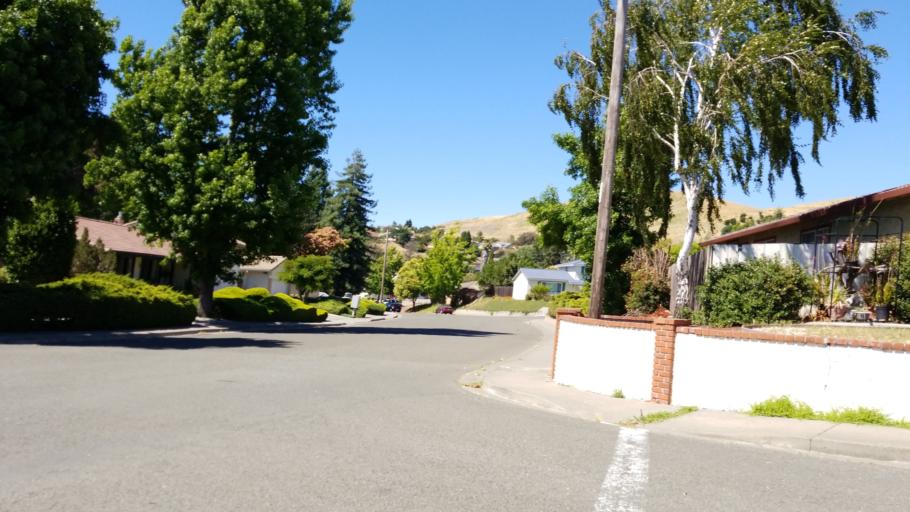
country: US
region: California
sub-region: Contra Costa County
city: Crockett
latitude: 38.0959
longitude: -122.1898
